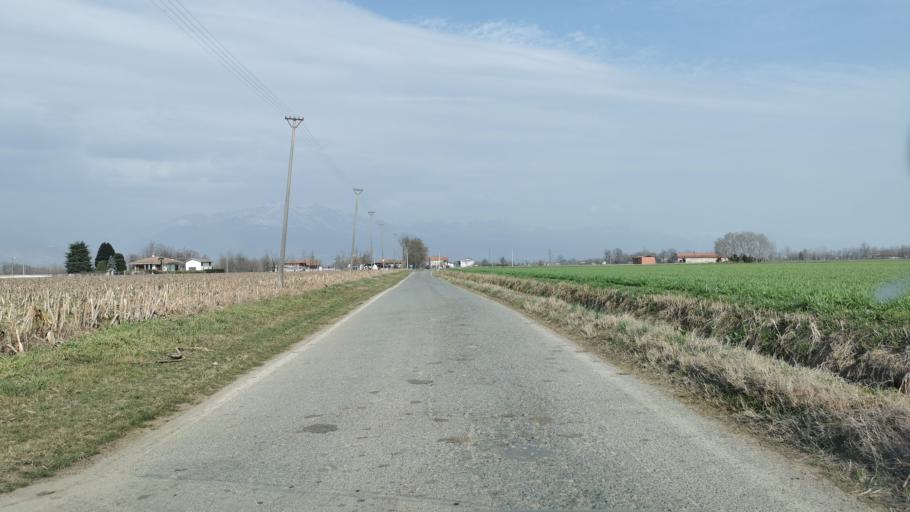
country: IT
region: Piedmont
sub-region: Provincia di Torino
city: Front
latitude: 45.2916
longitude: 7.6881
